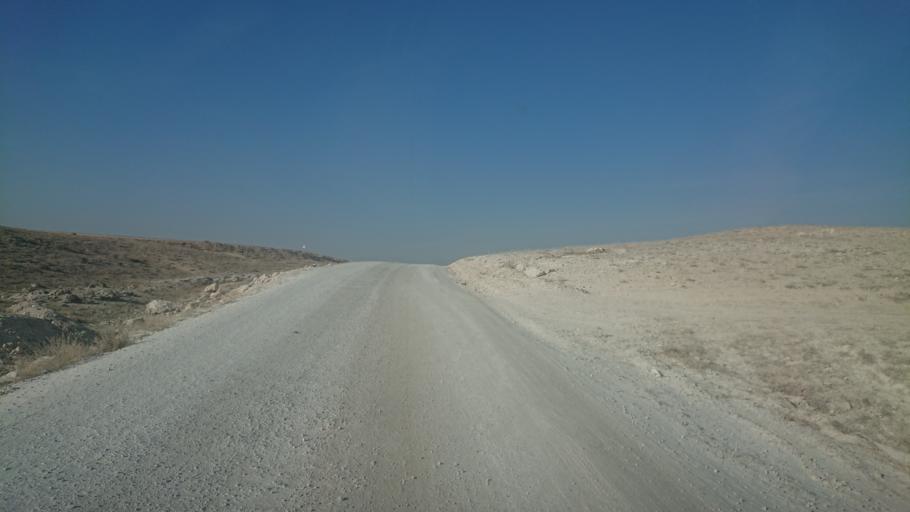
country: TR
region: Aksaray
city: Sultanhani
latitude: 38.0838
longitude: 33.6153
